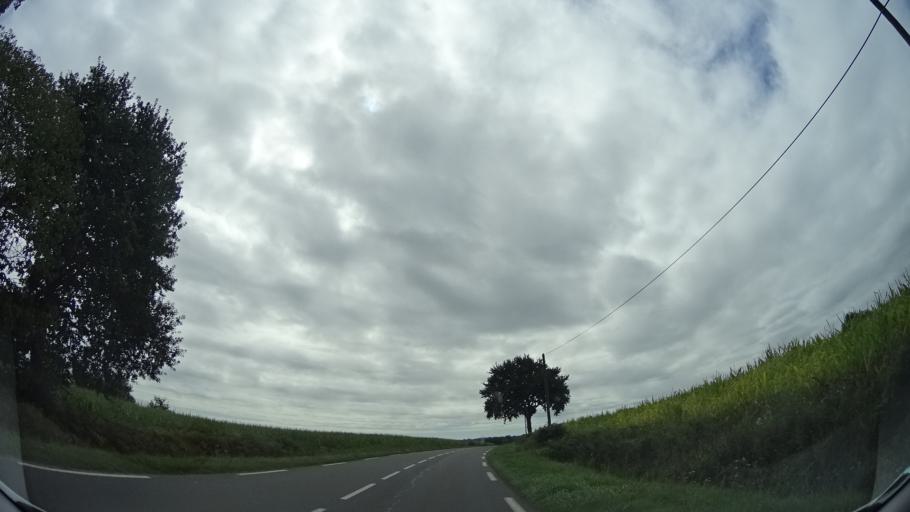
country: FR
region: Brittany
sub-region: Departement d'Ille-et-Vilaine
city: Hede-Bazouges
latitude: 48.2611
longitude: -1.8340
